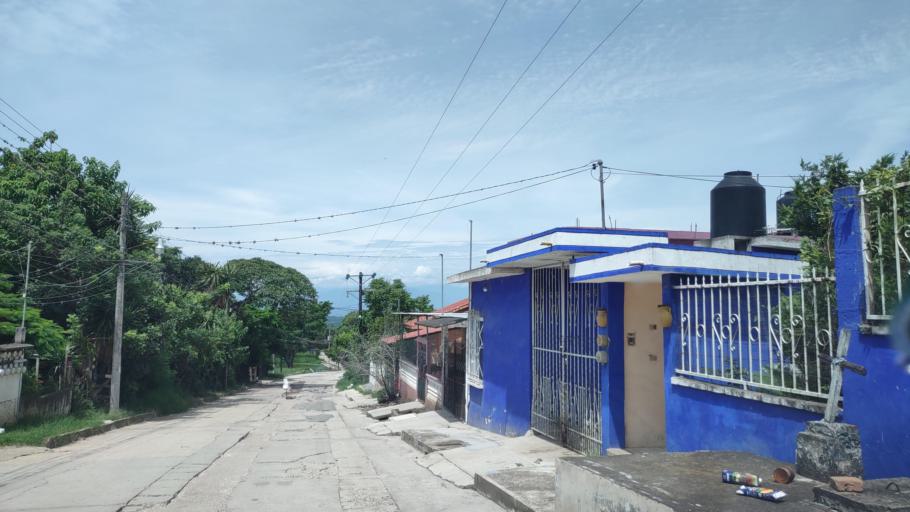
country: MX
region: Veracruz
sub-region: Emiliano Zapata
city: Jacarandas
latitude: 19.4679
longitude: -96.8318
